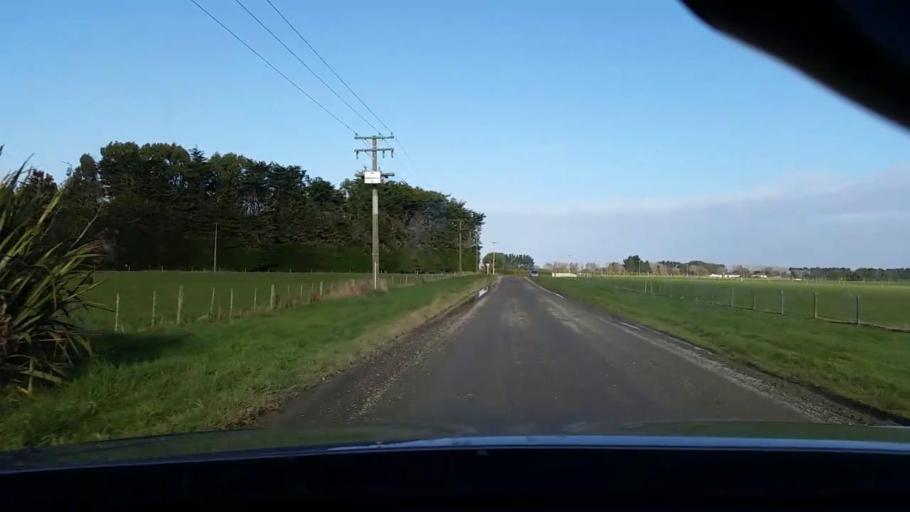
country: NZ
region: Southland
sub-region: Invercargill City
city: Invercargill
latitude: -46.3082
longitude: 168.3033
